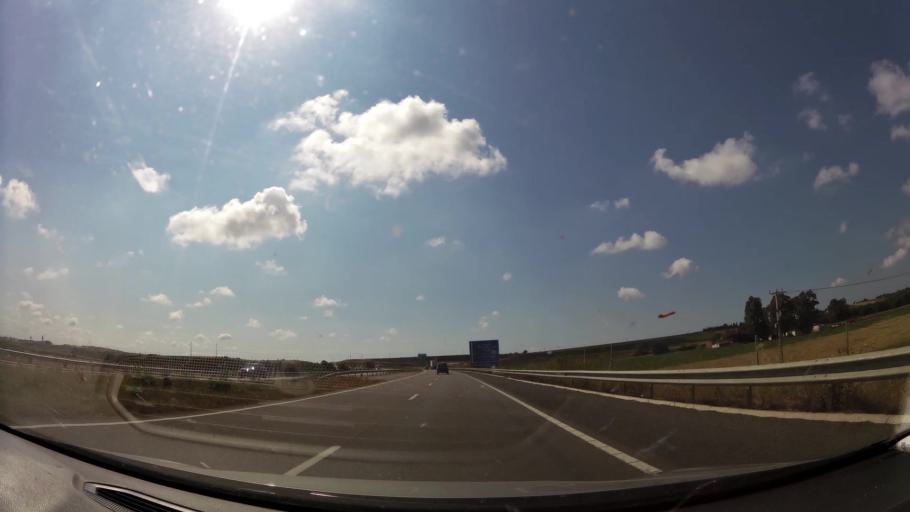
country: MA
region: Rabat-Sale-Zemmour-Zaer
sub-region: Skhirate-Temara
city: Temara
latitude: 33.8447
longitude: -6.8916
